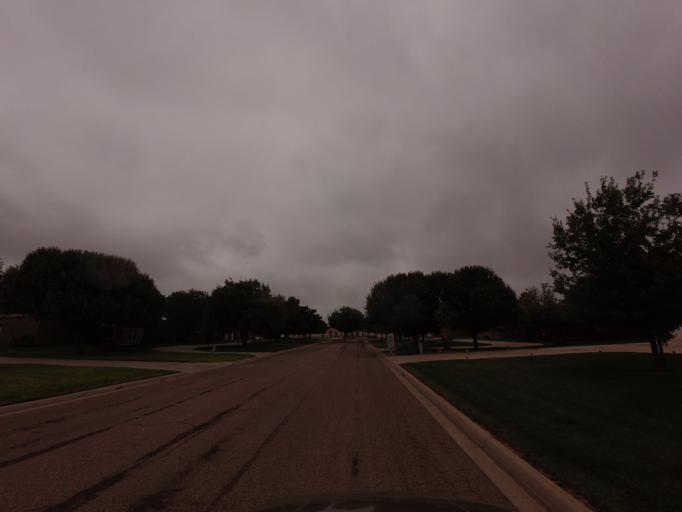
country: US
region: New Mexico
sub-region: Curry County
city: Clovis
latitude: 34.4319
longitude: -103.1835
